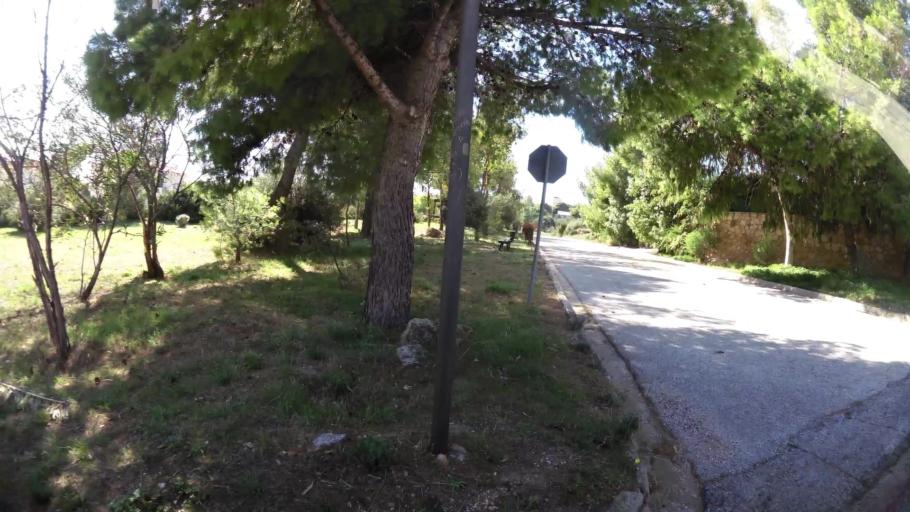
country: GR
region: Attica
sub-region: Nomarchia Anatolikis Attikis
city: Dhrafi
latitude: 38.0176
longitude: 23.9095
